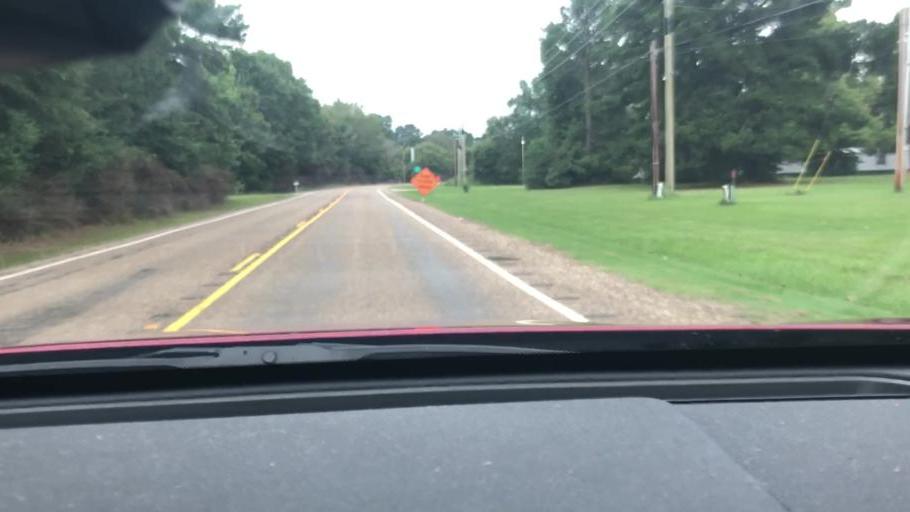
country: US
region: Texas
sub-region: Bowie County
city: Wake Village
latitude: 33.3825
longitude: -94.1058
